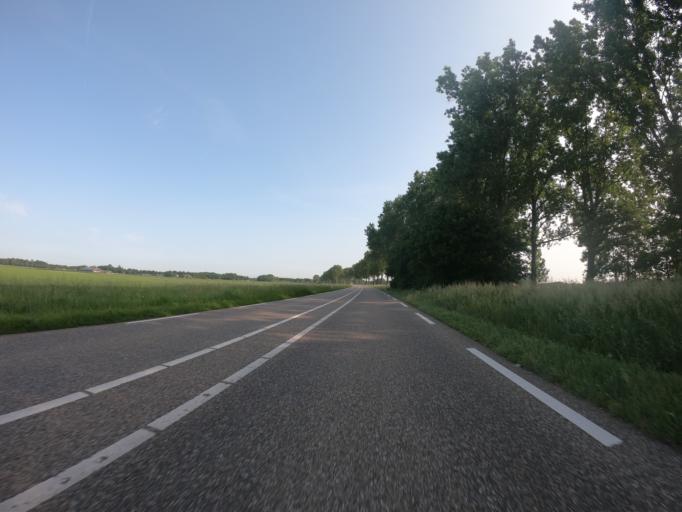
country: NL
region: North Brabant
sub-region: Gemeente Landerd
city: Reek
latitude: 51.7615
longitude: 5.6695
